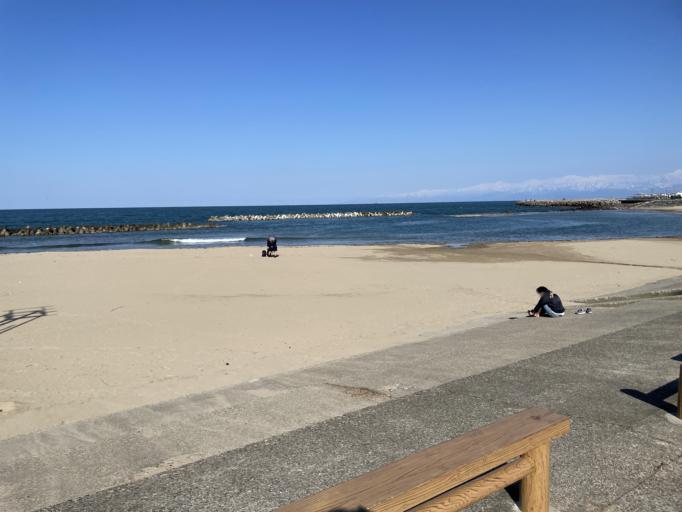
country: JP
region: Toyama
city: Himi
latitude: 36.8223
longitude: 137.0275
